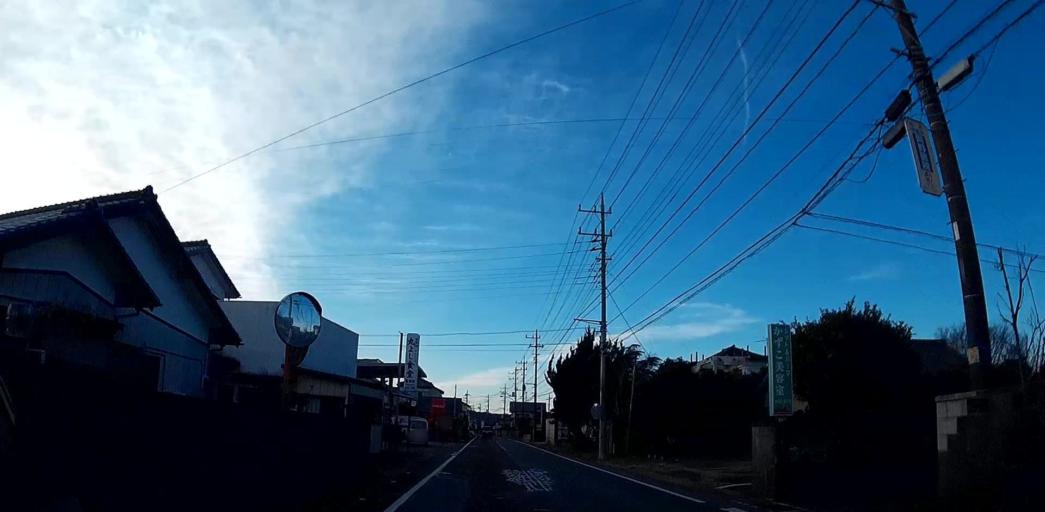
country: JP
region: Chiba
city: Omigawa
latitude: 35.8391
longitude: 140.6713
